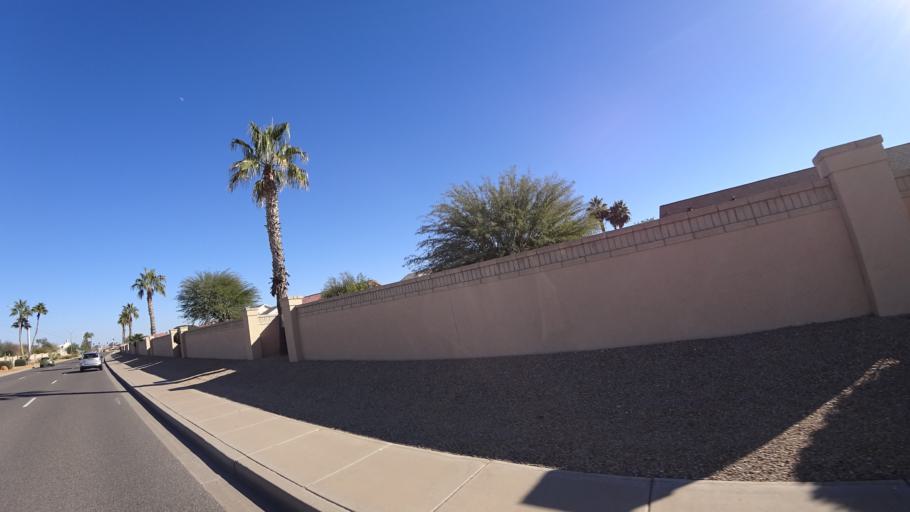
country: US
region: Arizona
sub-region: Maricopa County
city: Sun City West
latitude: 33.6721
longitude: -112.3834
